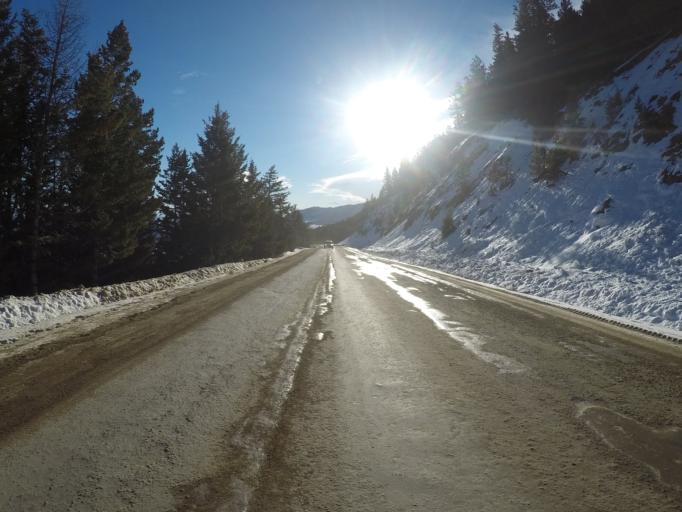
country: US
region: Montana
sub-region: Carbon County
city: Red Lodge
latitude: 45.1728
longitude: -109.3159
